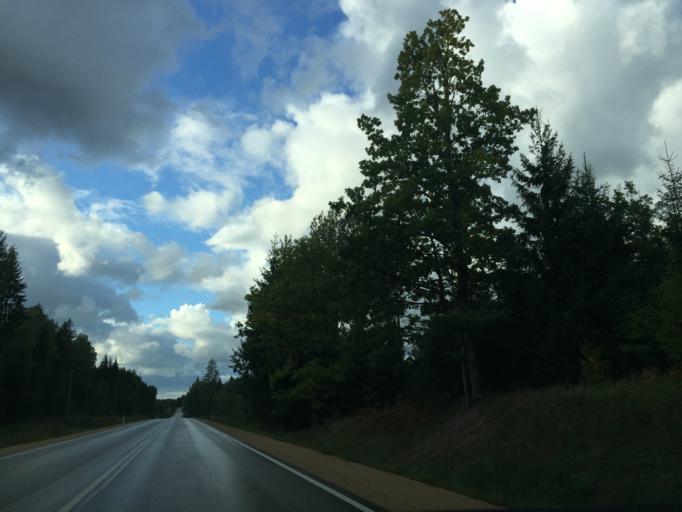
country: LV
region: Ligatne
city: Ligatne
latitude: 57.1565
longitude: 25.0650
